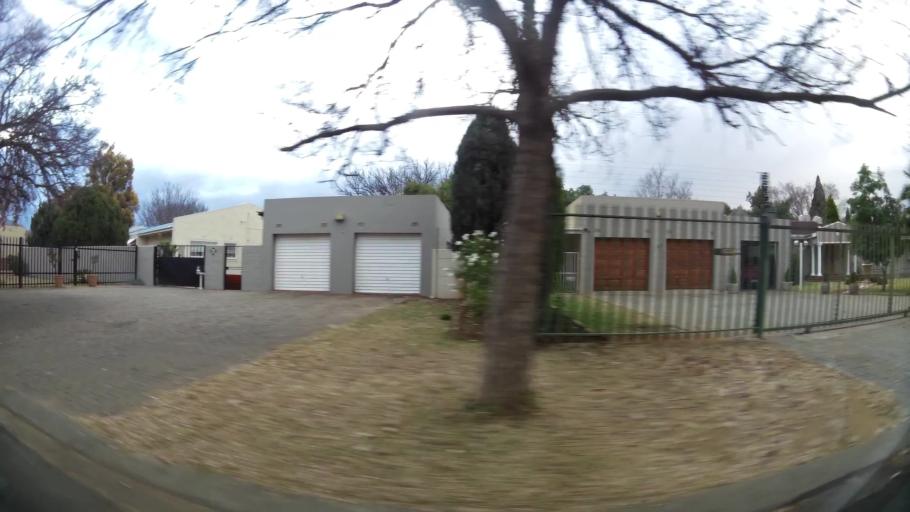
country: ZA
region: Orange Free State
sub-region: Lejweleputswa District Municipality
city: Welkom
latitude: -27.9552
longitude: 26.7406
